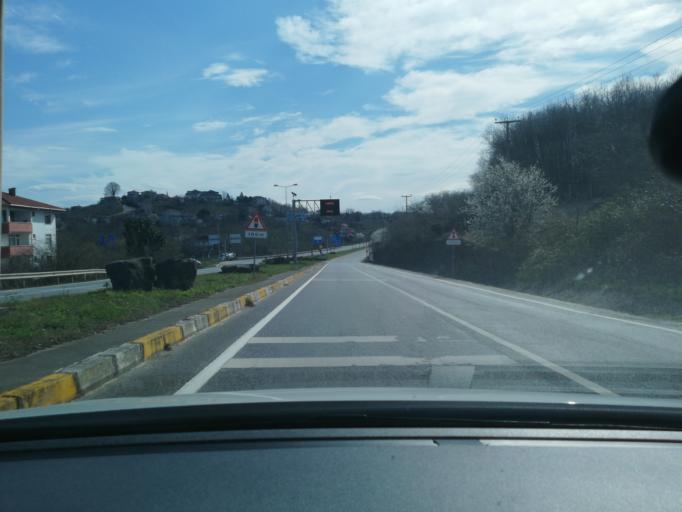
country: TR
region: Duzce
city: Akcakoca
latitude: 41.0866
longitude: 31.1519
